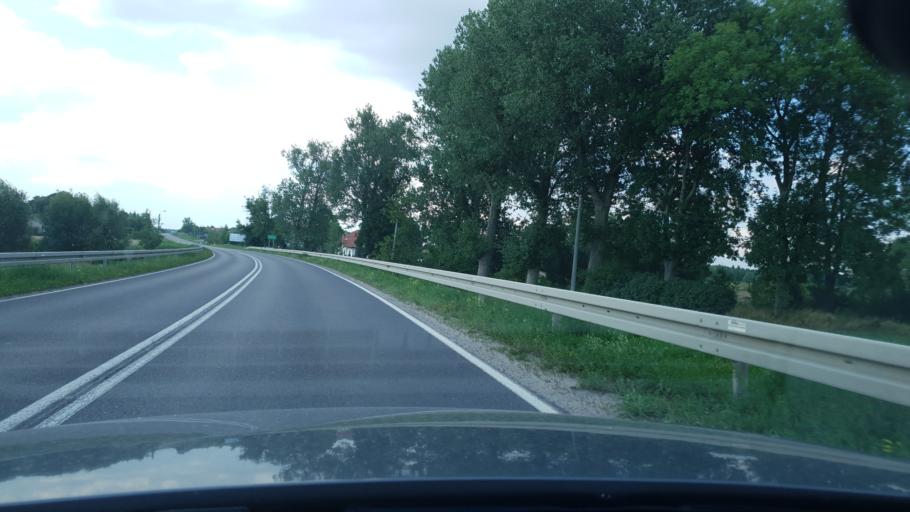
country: PL
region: Kujawsko-Pomorskie
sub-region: Powiat wabrzeski
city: Wabrzezno
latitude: 53.2817
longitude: 18.9296
